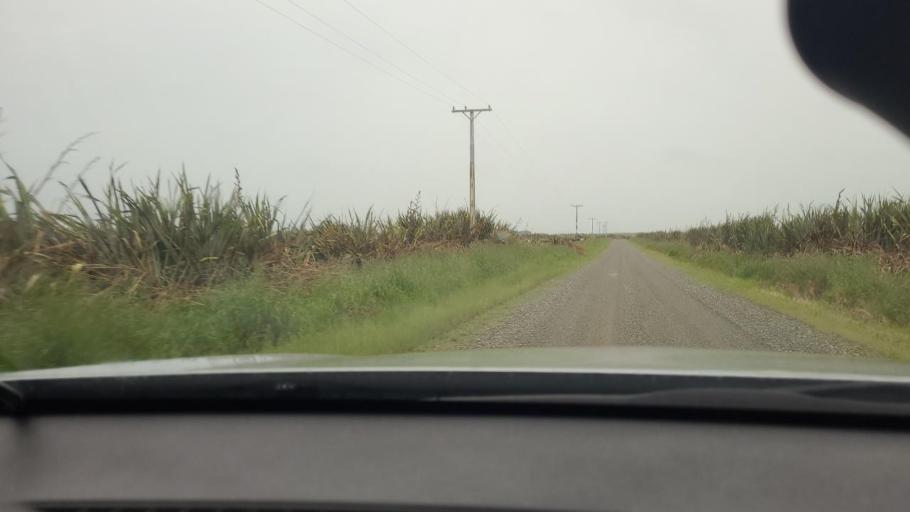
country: NZ
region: Southland
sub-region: Invercargill City
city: Invercargill
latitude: -46.3507
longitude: 168.2013
